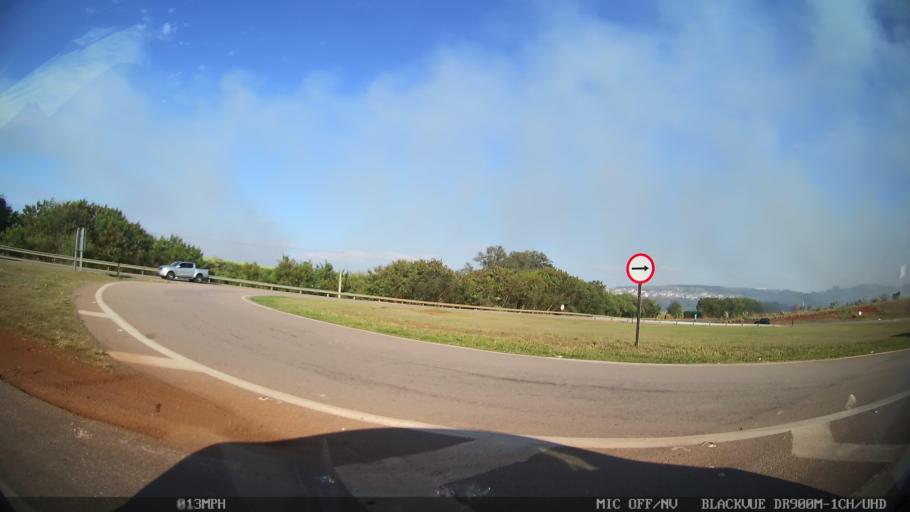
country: BR
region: Sao Paulo
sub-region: Piracicaba
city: Piracicaba
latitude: -22.6926
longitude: -47.6001
